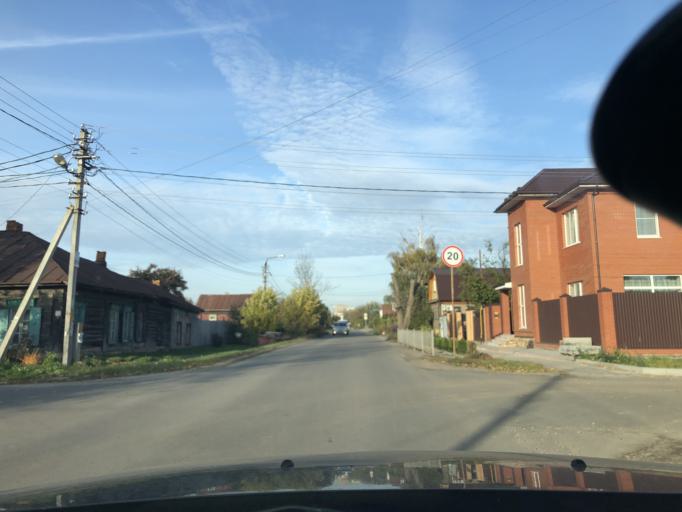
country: RU
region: Tula
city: Tula
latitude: 54.1863
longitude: 37.6356
